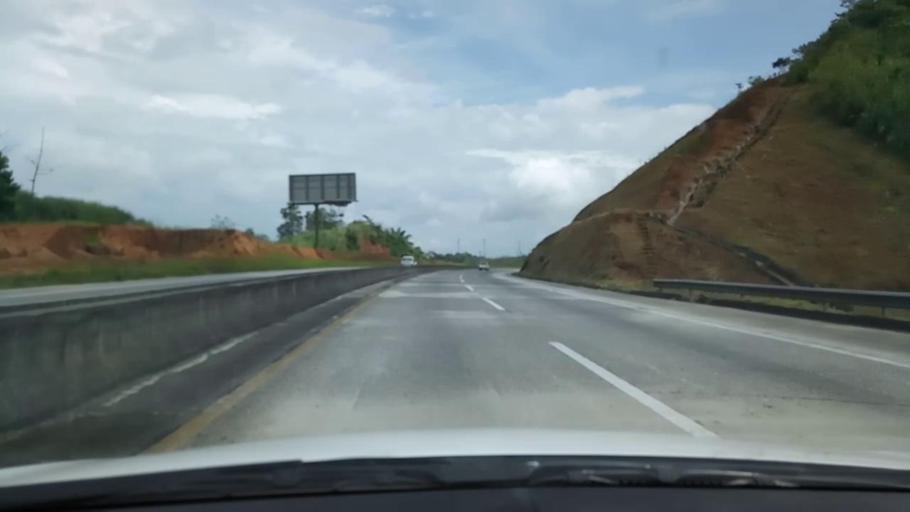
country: PA
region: Colon
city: Buena Vista
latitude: 9.2725
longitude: -79.7107
